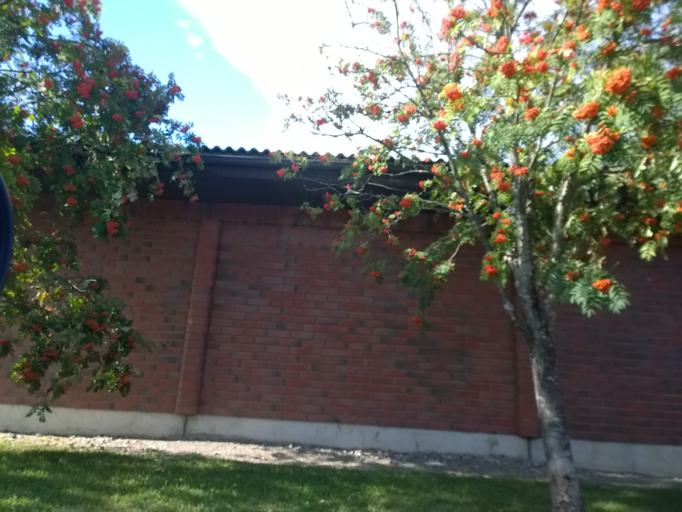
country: FI
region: Pirkanmaa
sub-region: Tampere
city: Tampere
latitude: 61.4644
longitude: 23.8561
